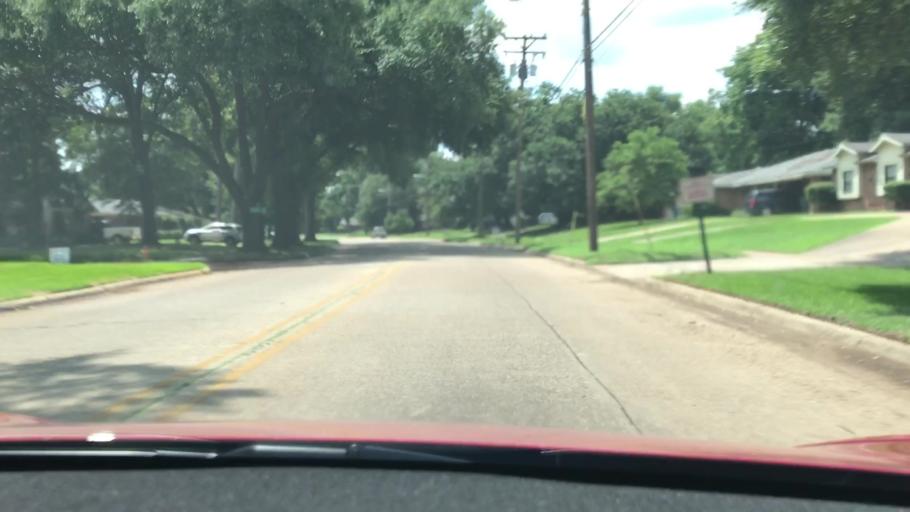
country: US
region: Louisiana
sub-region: Bossier Parish
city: Bossier City
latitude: 32.4604
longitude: -93.7348
